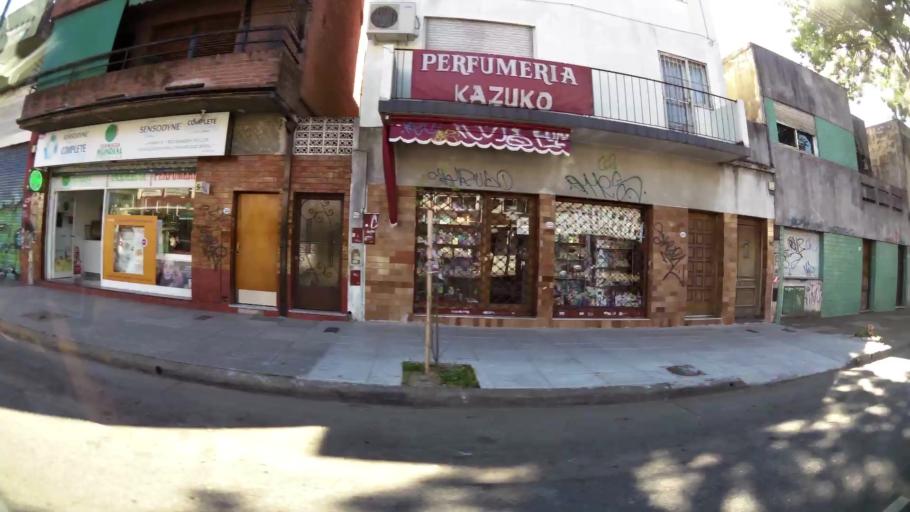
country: AR
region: Buenos Aires F.D.
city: Colegiales
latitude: -34.5592
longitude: -58.4736
